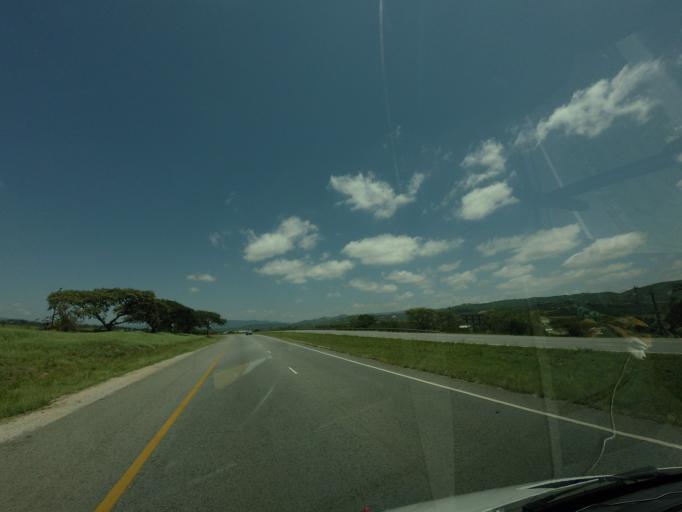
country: ZA
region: Mpumalanga
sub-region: Ehlanzeni District
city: Nelspruit
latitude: -25.4458
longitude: 30.8953
